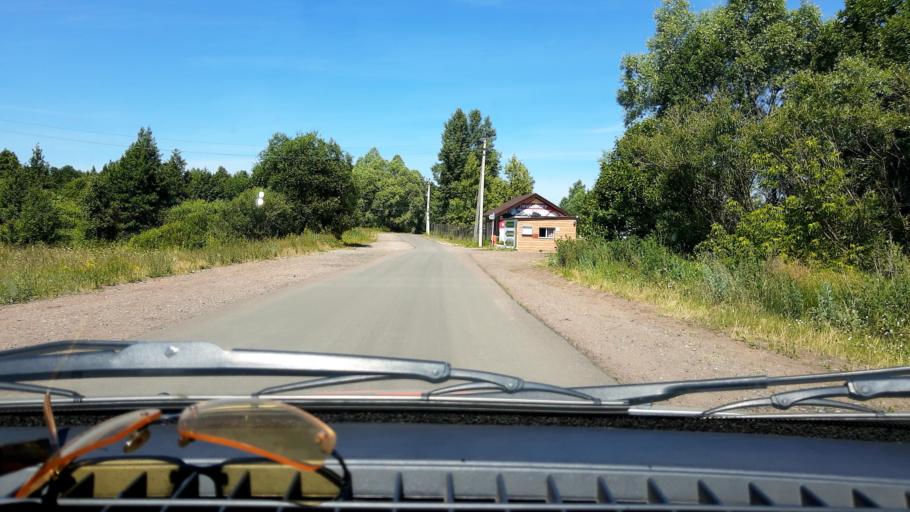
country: RU
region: Bashkortostan
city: Blagoveshchensk
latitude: 54.9672
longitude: 55.8135
